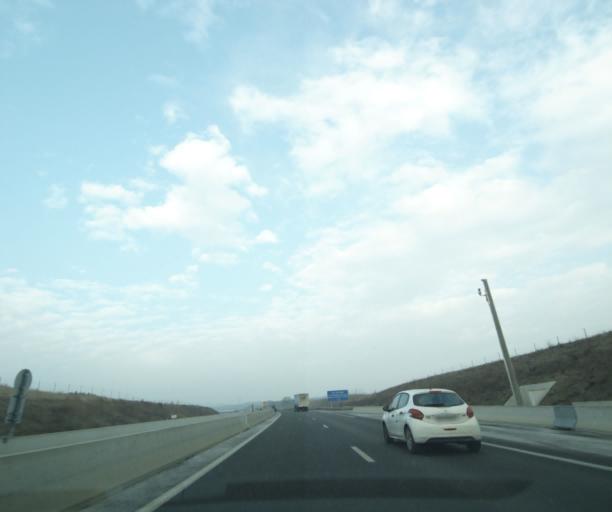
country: FR
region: Rhone-Alpes
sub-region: Departement du Rhone
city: Saint-Germain-Nuelles
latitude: 45.8595
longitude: 4.6425
